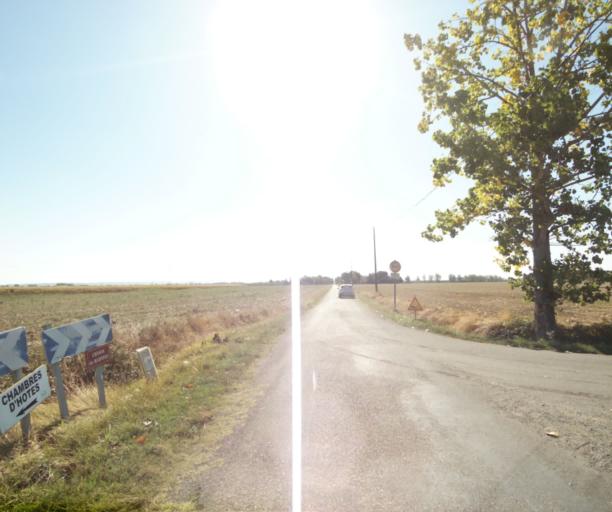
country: FR
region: Midi-Pyrenees
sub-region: Departement du Tarn-et-Garonne
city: Verdun-sur-Garonne
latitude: 43.8369
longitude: 1.2165
